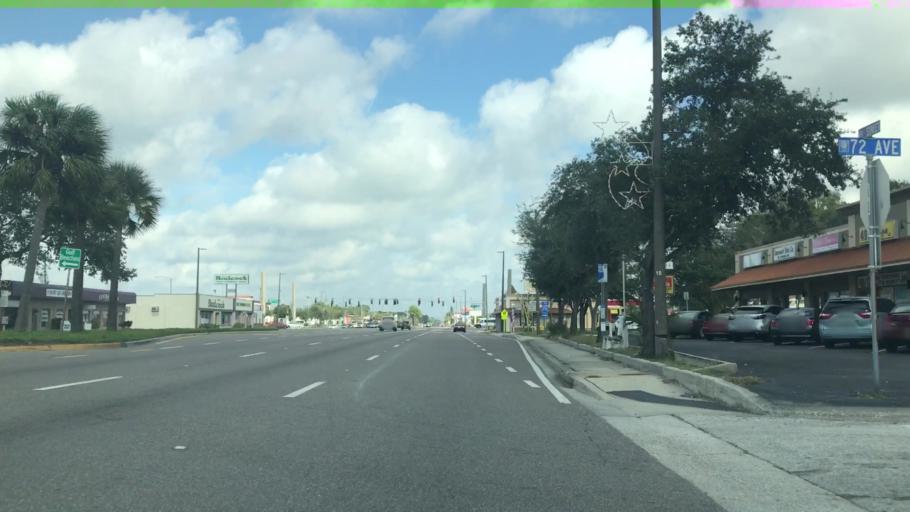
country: US
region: Florida
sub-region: Pinellas County
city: Pinellas Park
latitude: 27.8374
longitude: -82.6998
